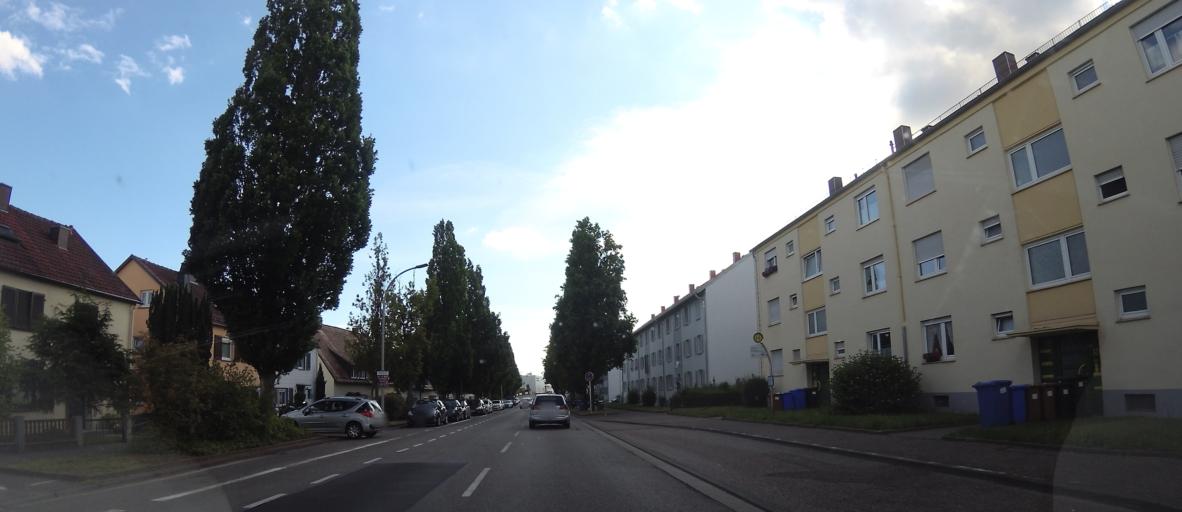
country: DE
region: Rheinland-Pfalz
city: Pirmasens
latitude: 49.1897
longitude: 7.5952
